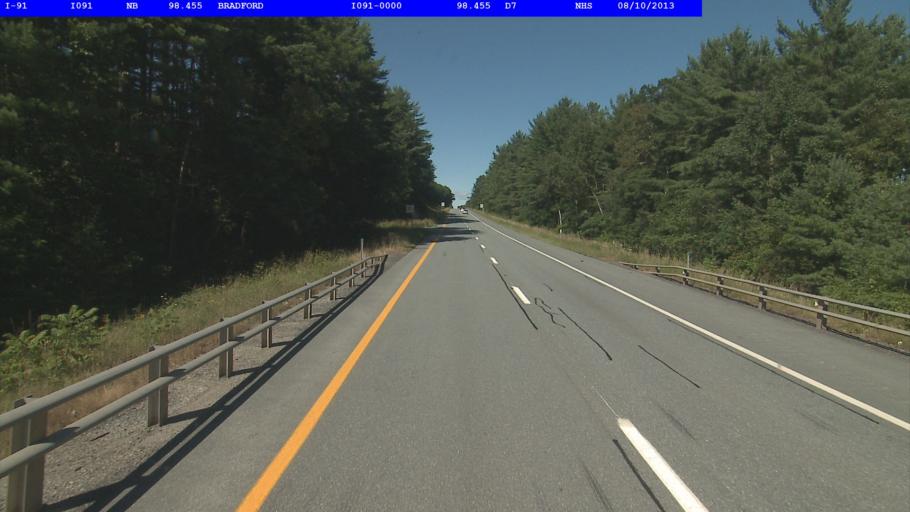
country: US
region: New Hampshire
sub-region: Grafton County
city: Haverhill
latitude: 43.9943
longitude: -72.1328
